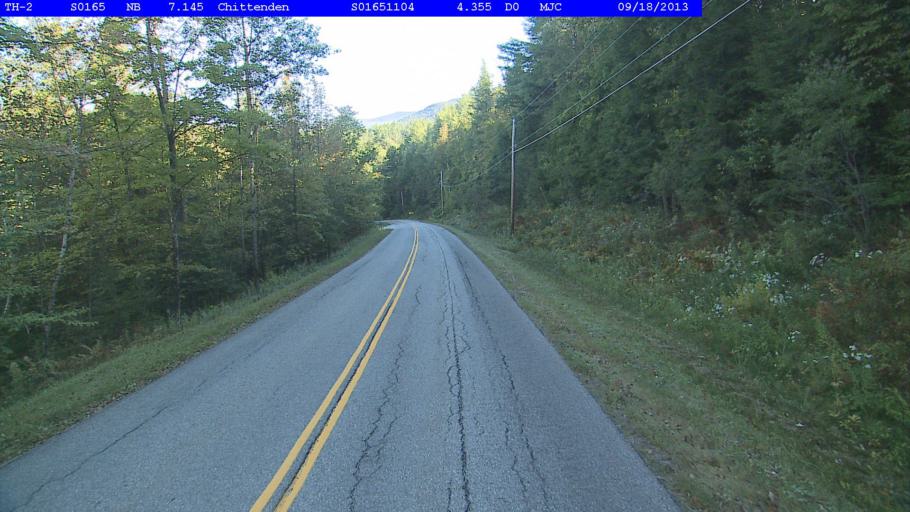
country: US
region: Vermont
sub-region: Rutland County
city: Rutland
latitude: 43.7366
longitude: -72.9707
